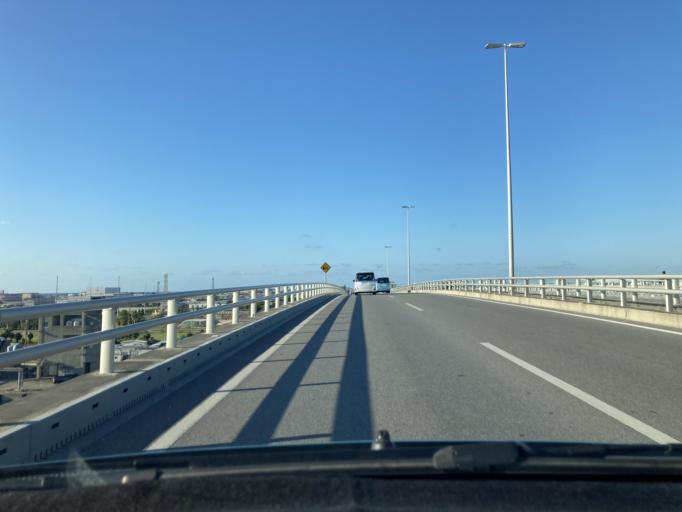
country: JP
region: Okinawa
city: Itoman
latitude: 26.1317
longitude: 127.6646
